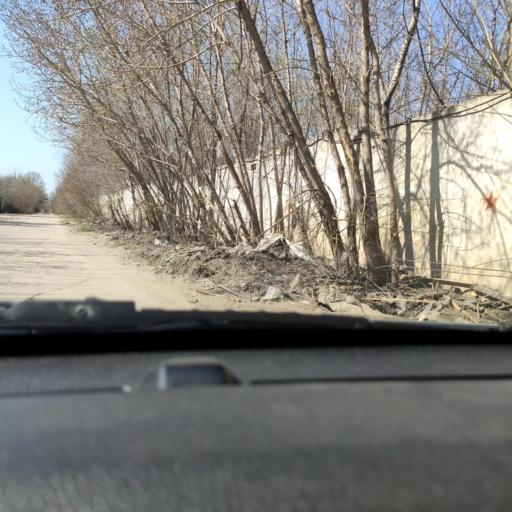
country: RU
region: Samara
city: Tol'yatti
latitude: 53.5366
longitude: 49.2571
